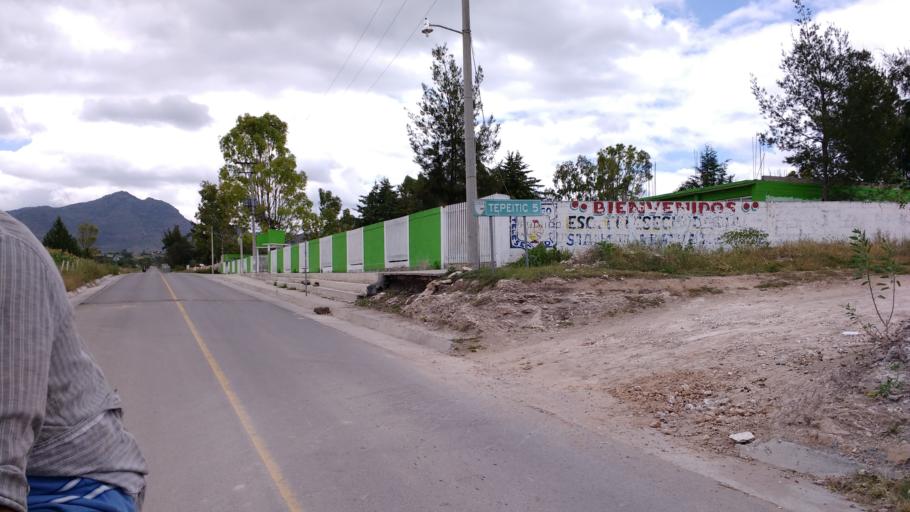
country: MX
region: Hidalgo
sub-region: Tezontepec de Aldama
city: Tenango
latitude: 20.2273
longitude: -99.2569
